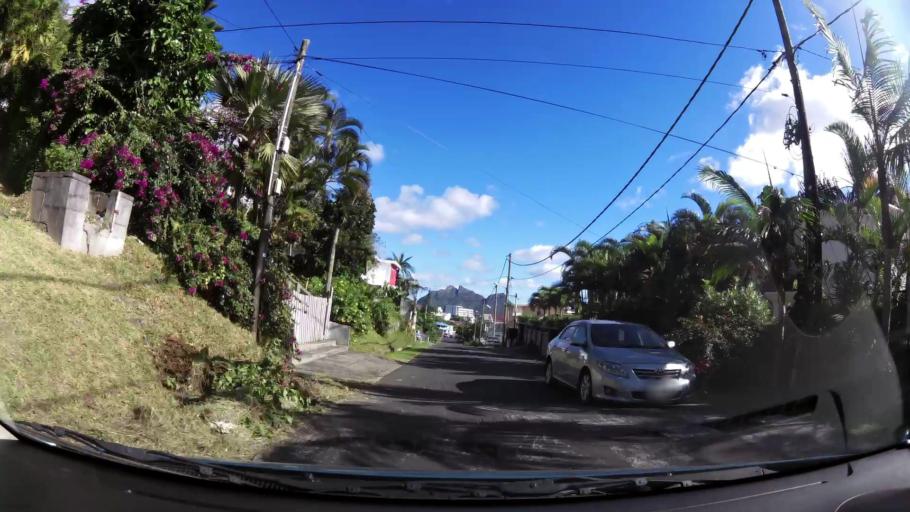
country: MU
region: Plaines Wilhems
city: Quatre Bornes
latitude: -20.2743
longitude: 57.4807
